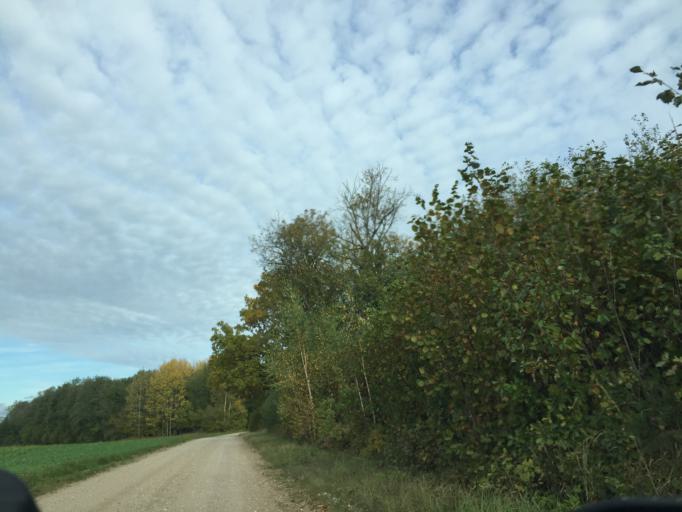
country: LV
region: Jaunpils
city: Jaunpils
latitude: 56.6435
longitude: 23.0770
